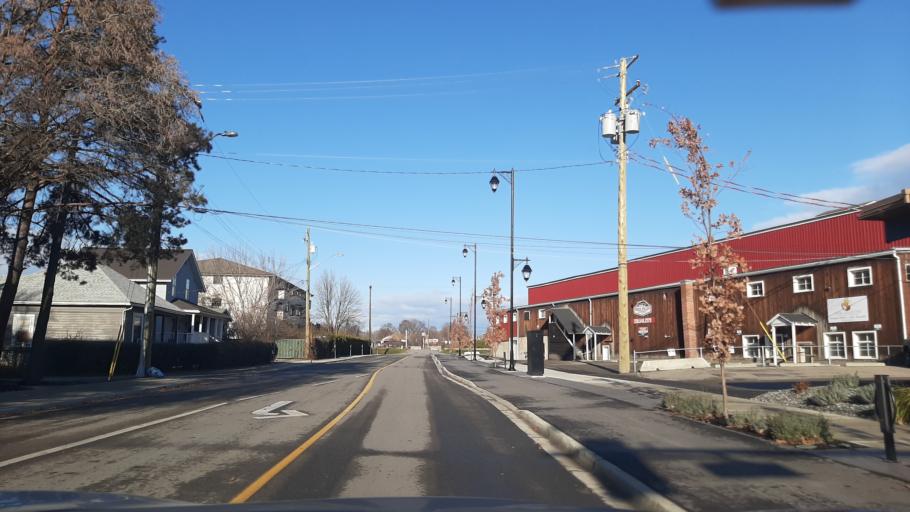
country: CA
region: British Columbia
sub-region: Regional District of North Okanagan
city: Vernon
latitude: 50.2675
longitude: -119.2708
